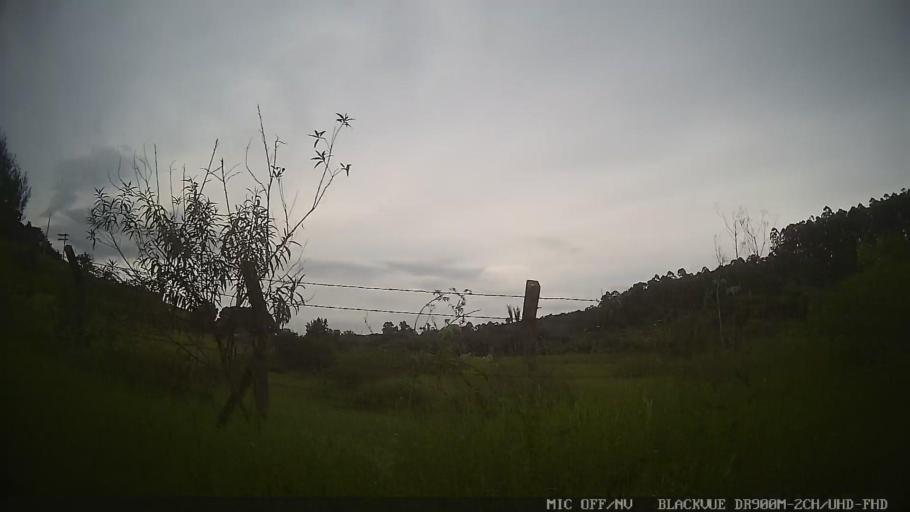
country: BR
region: Sao Paulo
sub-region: Atibaia
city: Atibaia
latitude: -23.1774
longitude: -46.5799
